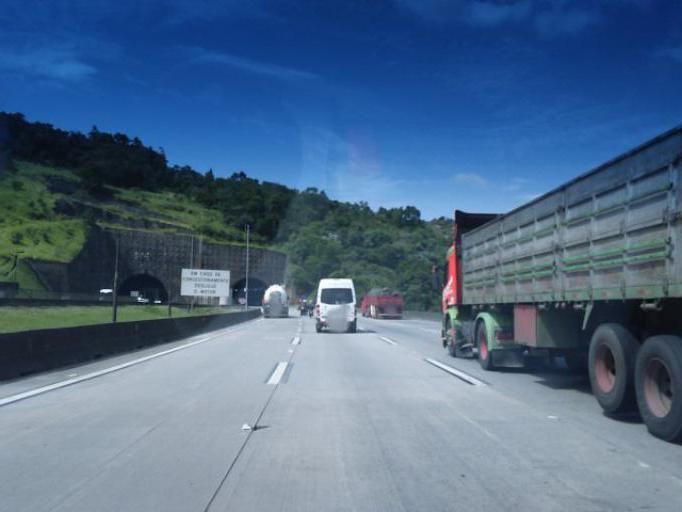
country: BR
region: Sao Paulo
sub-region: Taboao Da Serra
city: Taboao da Serra
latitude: -23.6189
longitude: -46.8281
